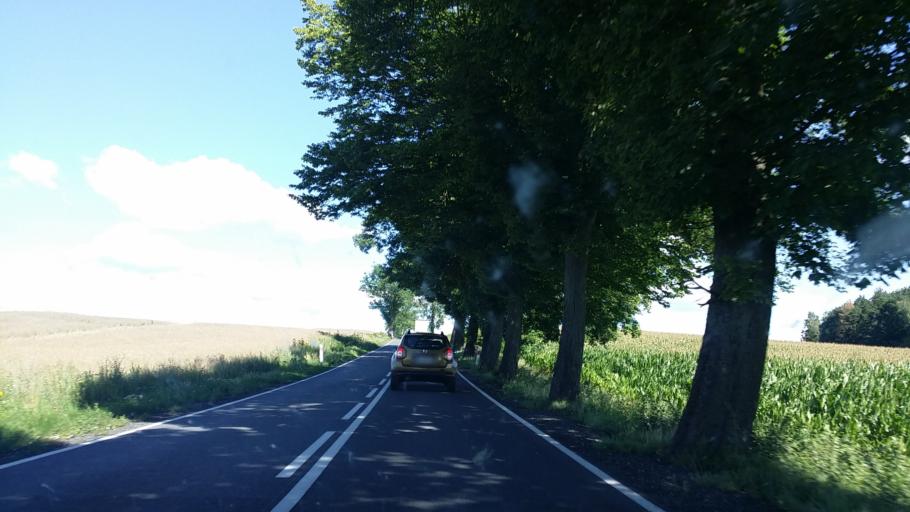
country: PL
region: West Pomeranian Voivodeship
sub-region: Powiat drawski
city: Kalisz Pomorski
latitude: 53.3190
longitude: 15.9046
